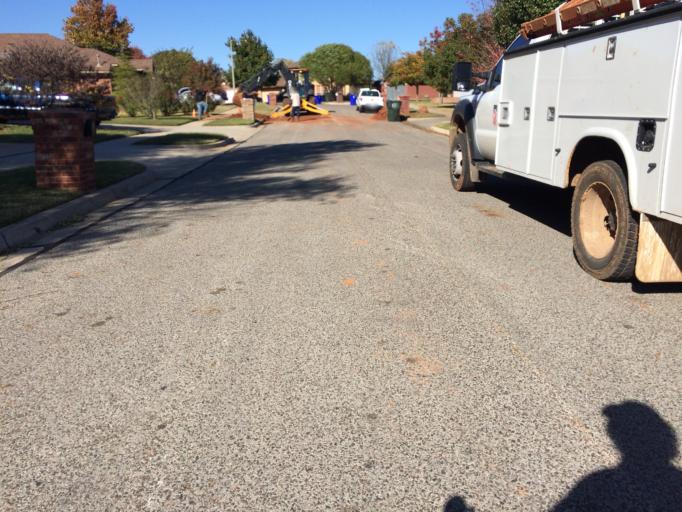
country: US
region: Oklahoma
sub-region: Cleveland County
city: Noble
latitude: 35.1693
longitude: -97.4270
